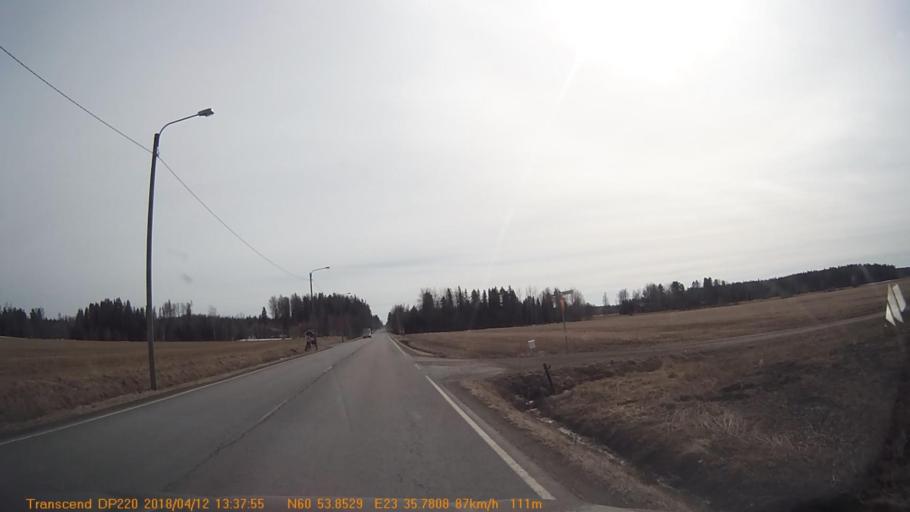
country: FI
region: Haeme
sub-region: Forssa
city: Forssa
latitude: 60.8971
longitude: 23.5965
